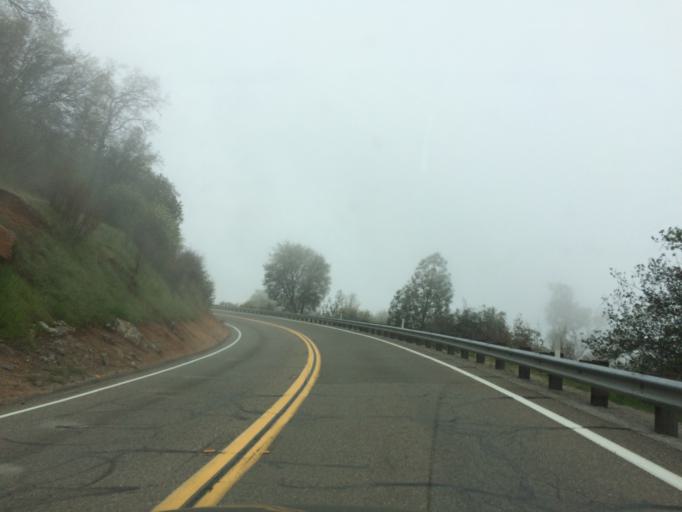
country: US
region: California
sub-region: Mariposa County
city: Mariposa
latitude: 37.4757
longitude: -120.0749
